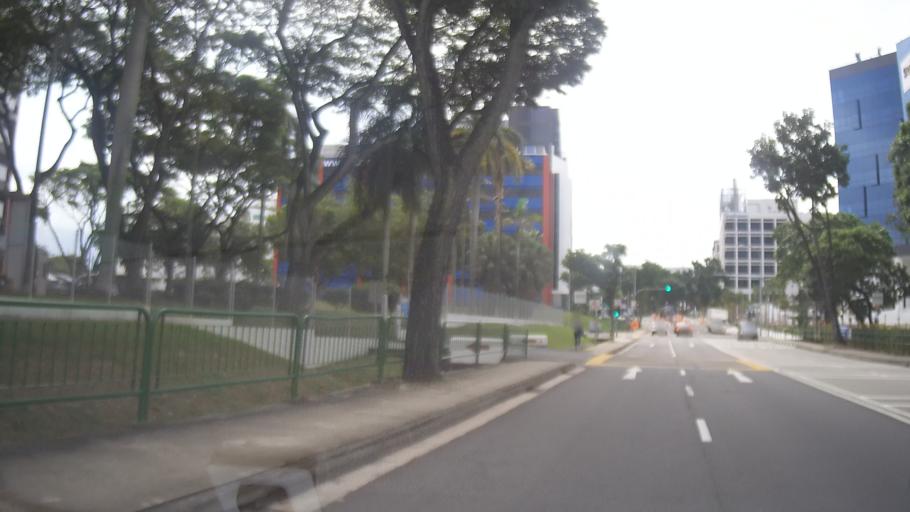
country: SG
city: Singapore
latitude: 1.3224
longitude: 103.8755
